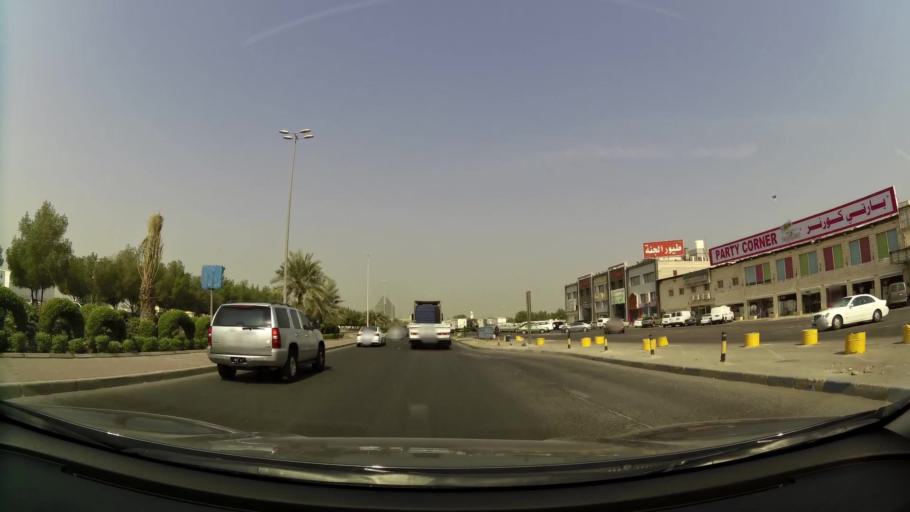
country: KW
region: Al Asimah
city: Ar Rabiyah
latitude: 29.3206
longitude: 47.9243
